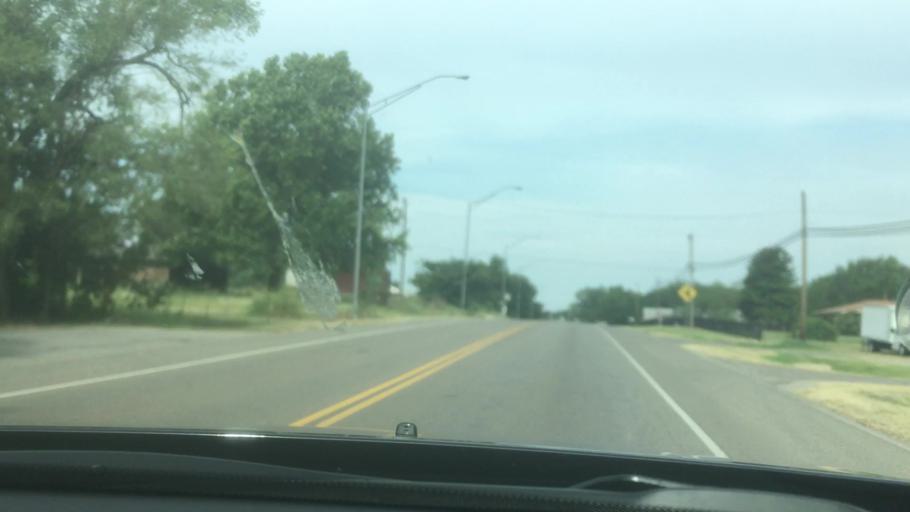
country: US
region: Oklahoma
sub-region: Garvin County
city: Maysville
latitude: 34.8173
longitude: -97.4179
